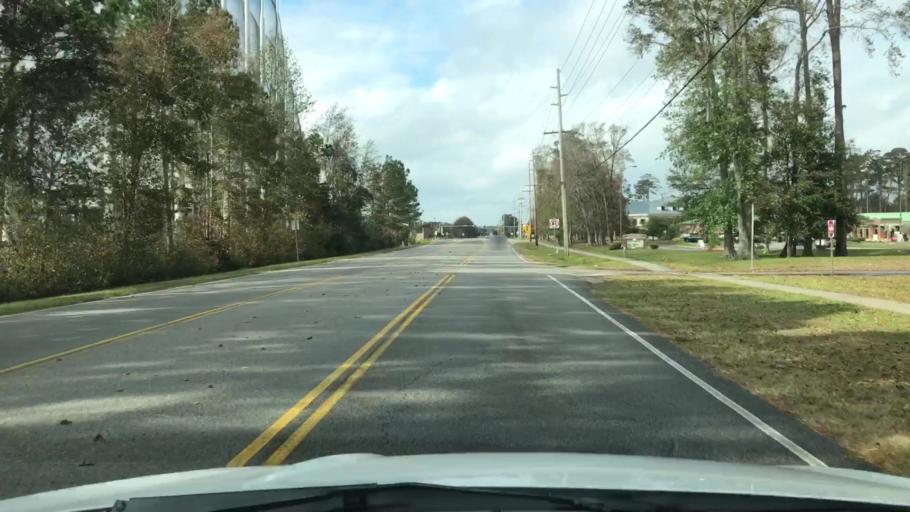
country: US
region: South Carolina
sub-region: Horry County
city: Myrtle Beach
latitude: 33.7134
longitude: -78.8697
